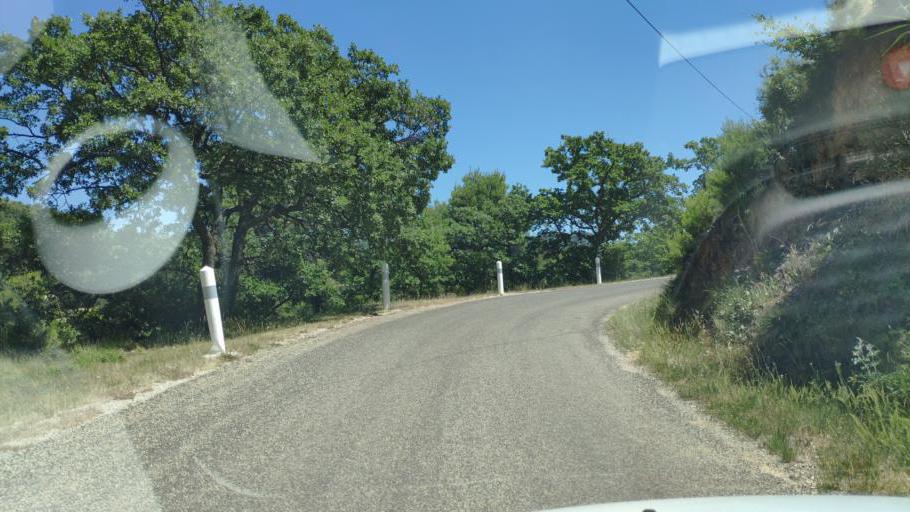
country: FR
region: Provence-Alpes-Cote d'Azur
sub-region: Departement du Vaucluse
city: Malaucene
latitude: 44.1767
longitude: 5.0760
